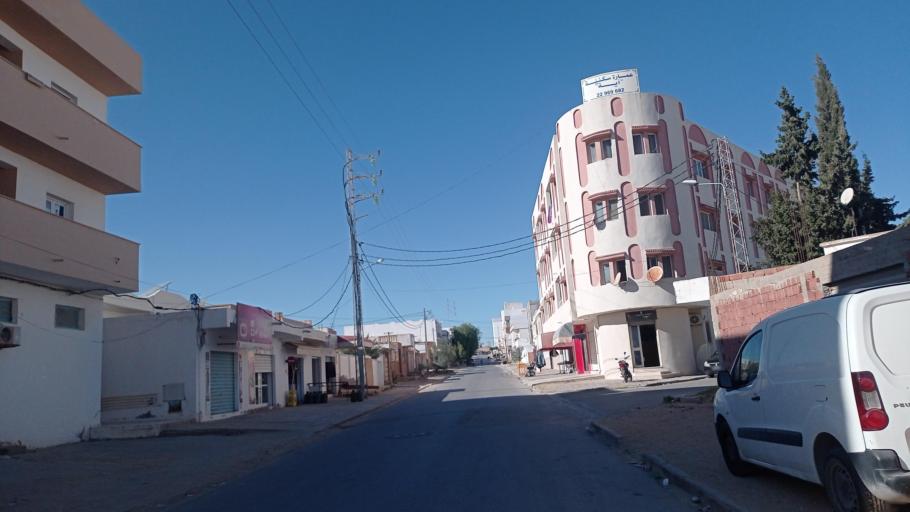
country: TN
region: Qabis
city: Gabes
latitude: 33.8451
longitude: 10.1129
